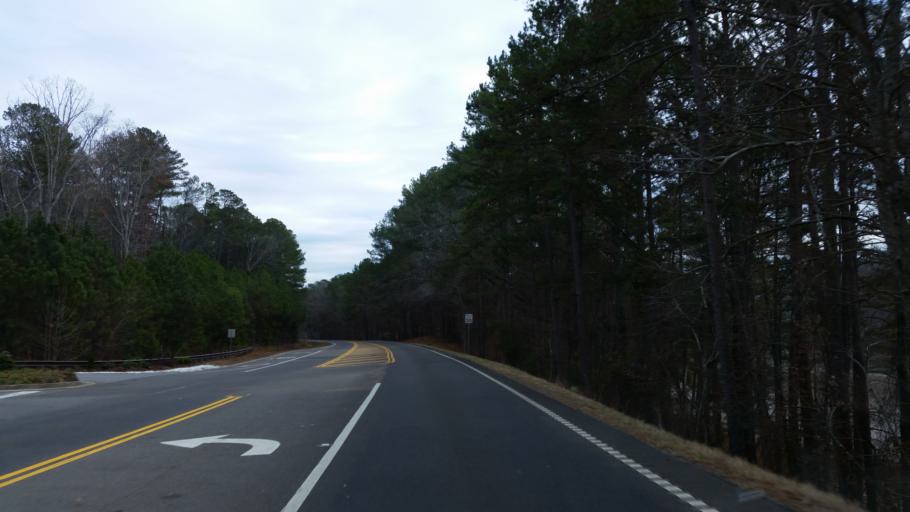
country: US
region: Georgia
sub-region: Cherokee County
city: Holly Springs
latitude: 34.2162
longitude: -84.5712
